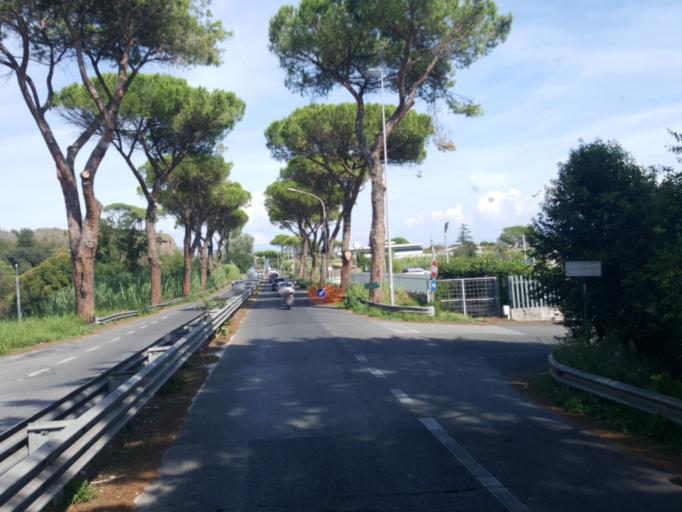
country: VA
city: Vatican City
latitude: 41.9550
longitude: 12.4787
